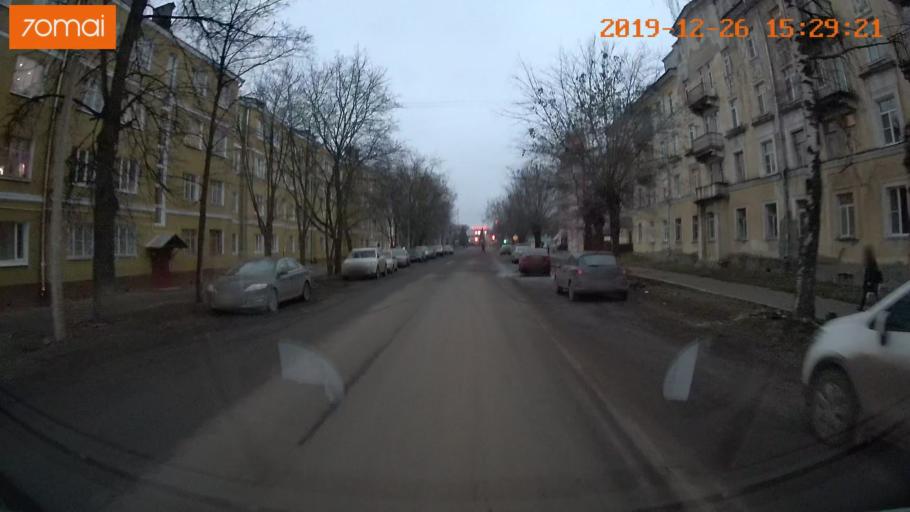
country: RU
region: Jaroslavl
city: Rybinsk
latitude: 58.0573
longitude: 38.8168
